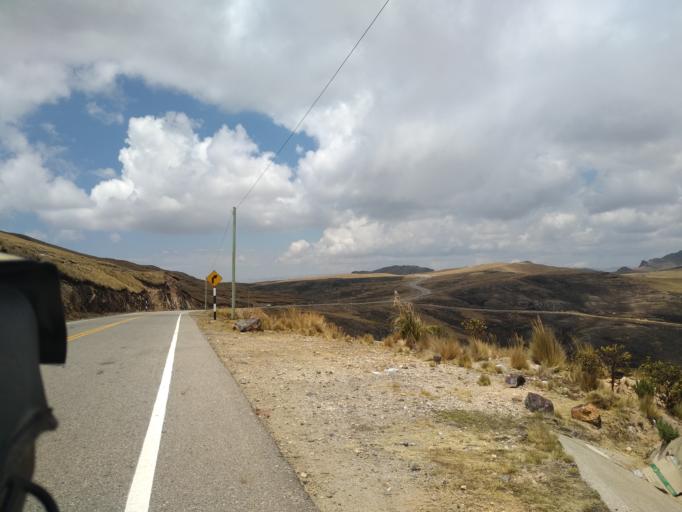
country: PE
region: La Libertad
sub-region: Provincia de Santiago de Chuco
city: Quiruvilca
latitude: -7.9573
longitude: -78.1958
